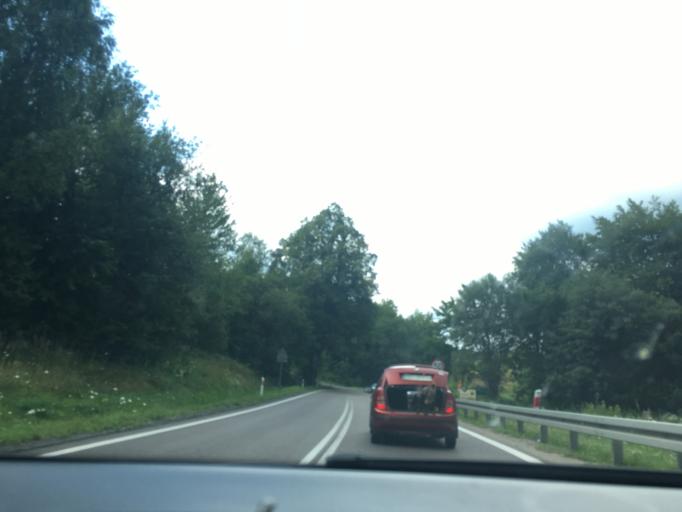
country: PL
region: Subcarpathian Voivodeship
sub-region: Powiat brzozowski
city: Jablonica Polska
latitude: 49.7302
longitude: 21.9072
